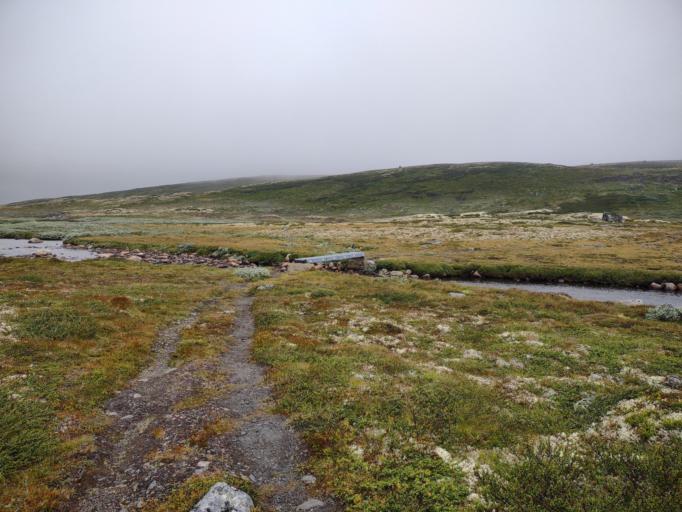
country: NO
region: Buskerud
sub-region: Hol
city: Geilo
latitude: 60.3960
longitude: 7.6558
